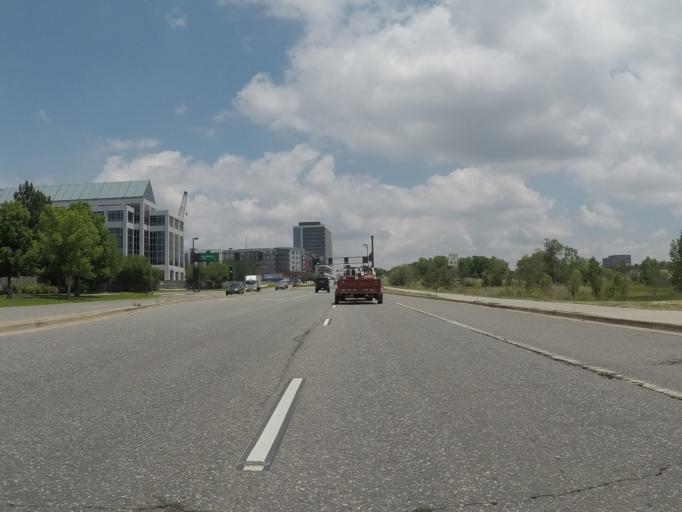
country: US
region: Colorado
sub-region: Arapahoe County
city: Greenwood Village
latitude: 39.6241
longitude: -104.9131
